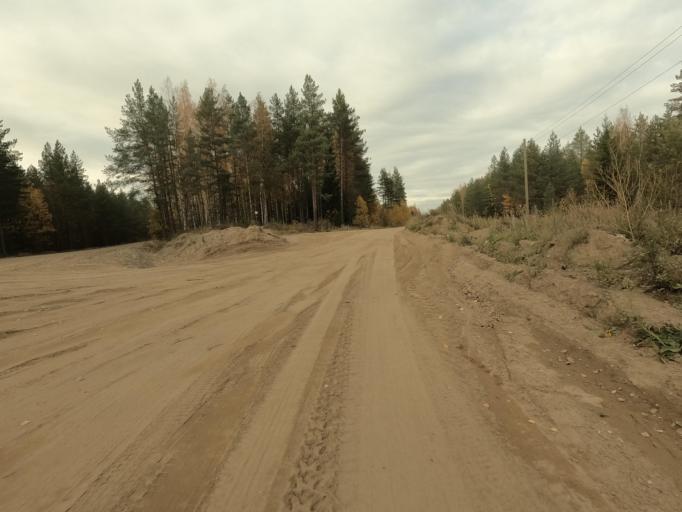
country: RU
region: Leningrad
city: Priladozhskiy
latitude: 59.6887
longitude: 31.3604
